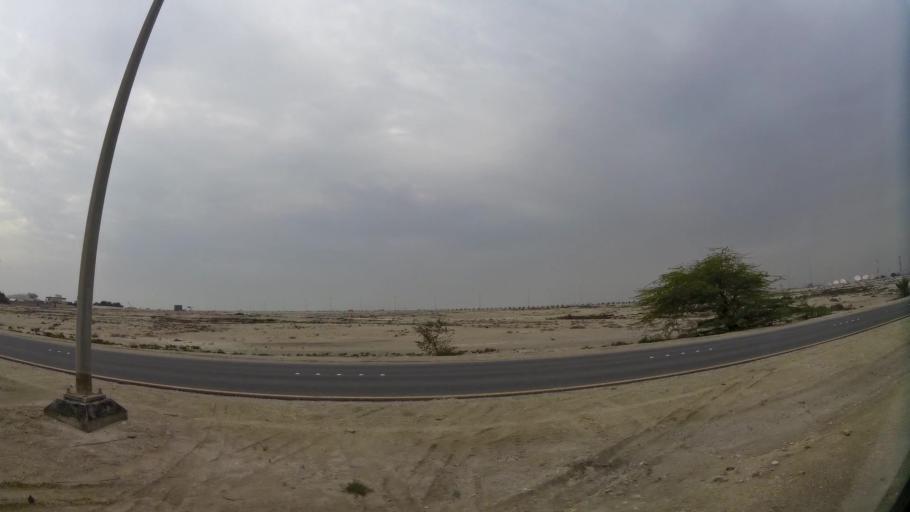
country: BH
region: Northern
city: Ar Rifa'
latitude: 26.0645
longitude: 50.6169
